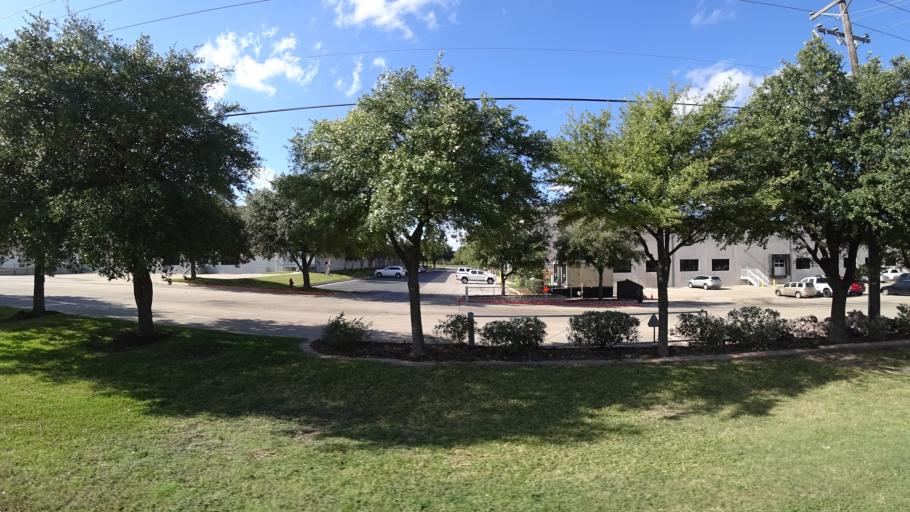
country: US
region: Texas
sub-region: Travis County
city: Wells Branch
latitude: 30.4721
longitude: -97.6733
